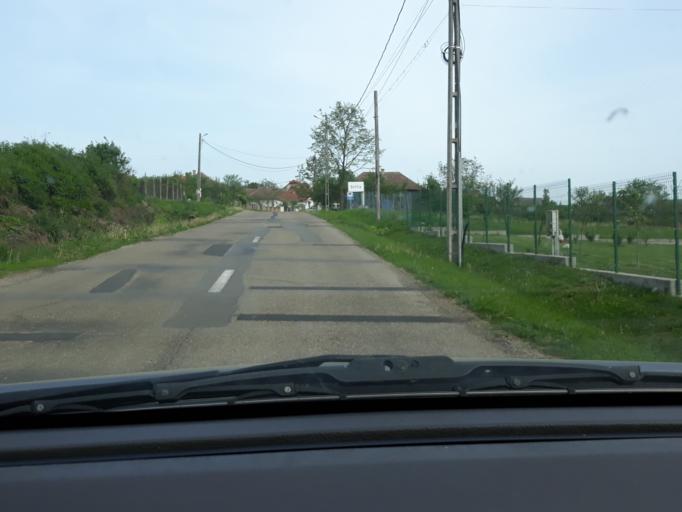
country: RO
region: Bihor
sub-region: Comuna Sanmartin
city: Sanmartin
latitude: 46.9755
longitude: 22.0086
